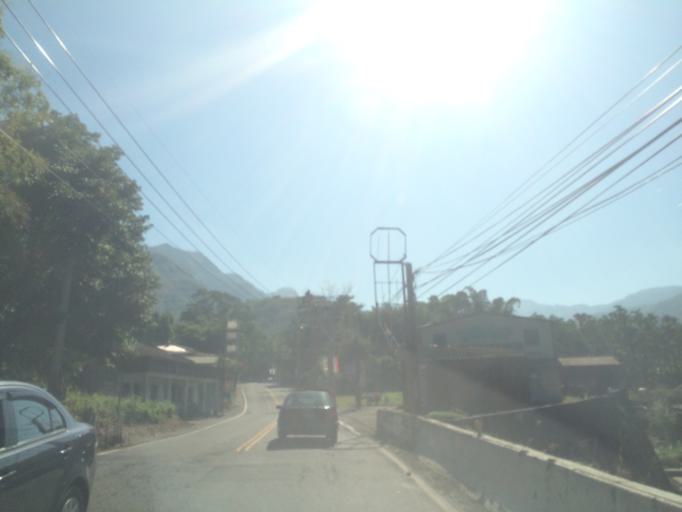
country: TW
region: Taiwan
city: Lugu
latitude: 23.7248
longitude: 120.7765
